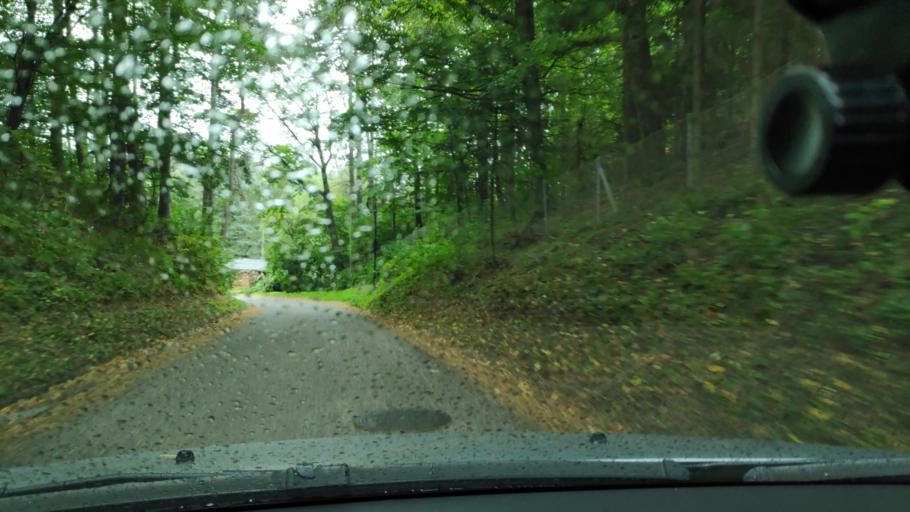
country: AT
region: Lower Austria
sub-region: Politischer Bezirk Neunkirchen
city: Grunbach am Schneeberg
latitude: 47.8048
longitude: 15.9910
